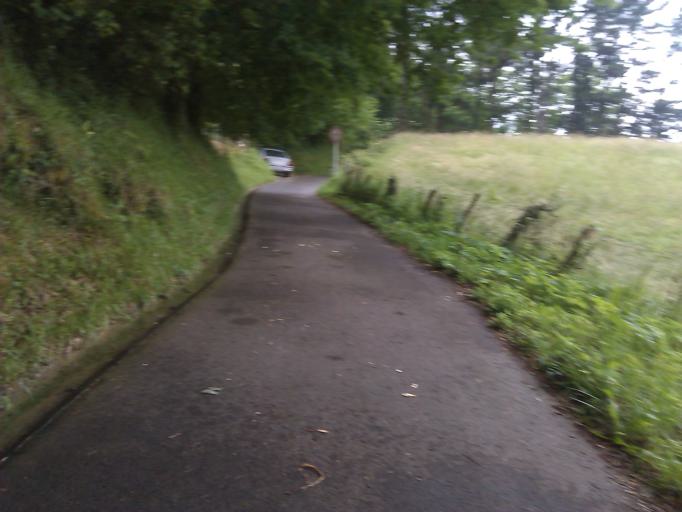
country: ES
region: Basque Country
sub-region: Provincia de Guipuzcoa
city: Hernani
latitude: 43.2591
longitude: -1.9765
